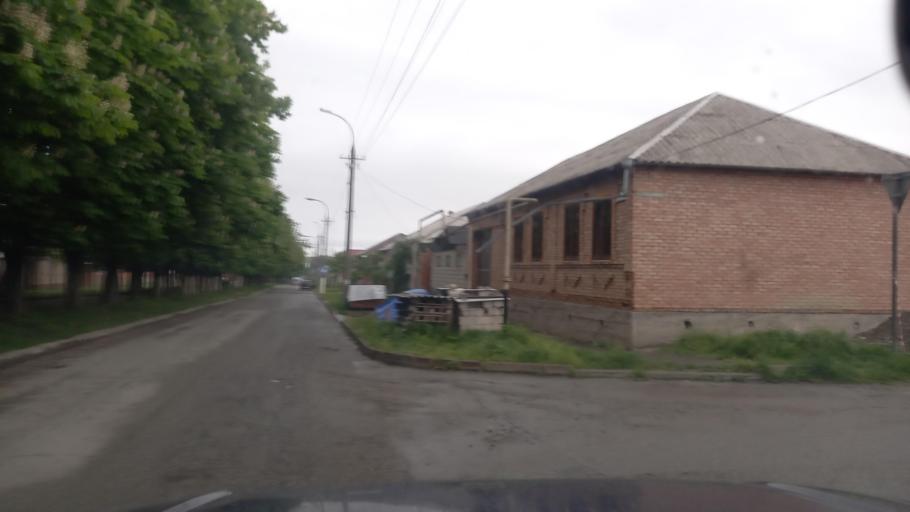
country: RU
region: North Ossetia
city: Alagir
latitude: 43.0458
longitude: 44.2207
